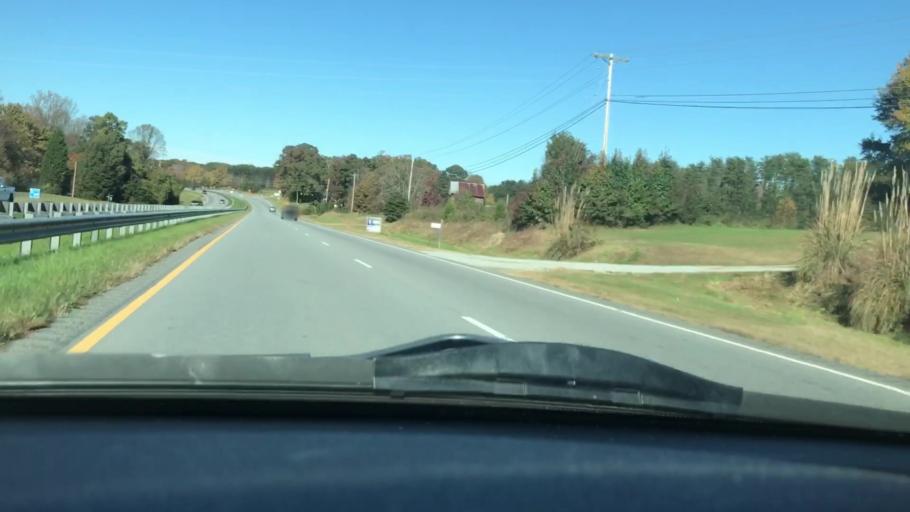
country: US
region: North Carolina
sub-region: Rockingham County
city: Madison
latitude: 36.3346
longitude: -79.9451
